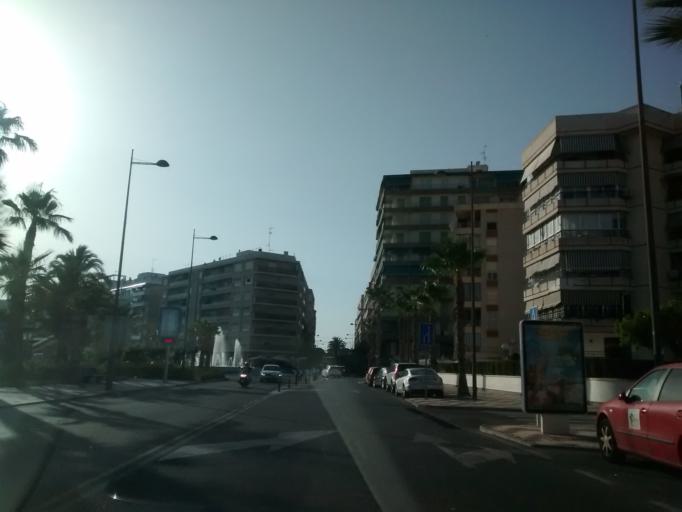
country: ES
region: Valencia
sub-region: Provincia de Alicante
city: Santa Pola
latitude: 38.1913
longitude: -0.5593
